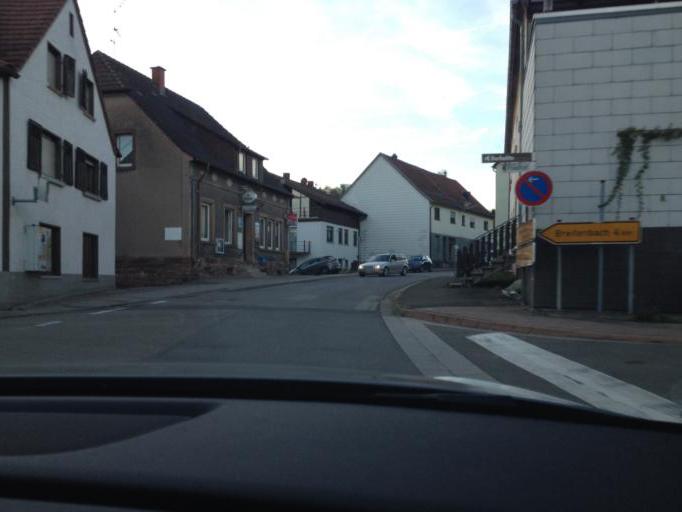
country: DE
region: Rheinland-Pfalz
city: Altenkirchen
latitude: 49.4428
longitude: 7.3229
